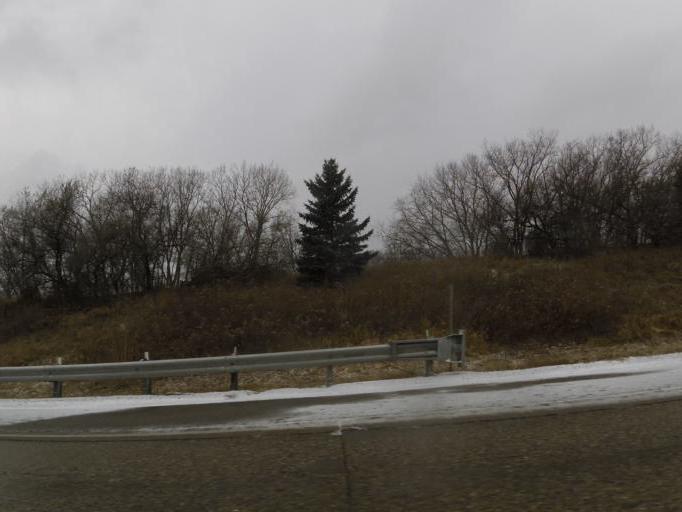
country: US
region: Minnesota
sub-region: Dakota County
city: Eagan
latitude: 44.7985
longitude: -93.2222
